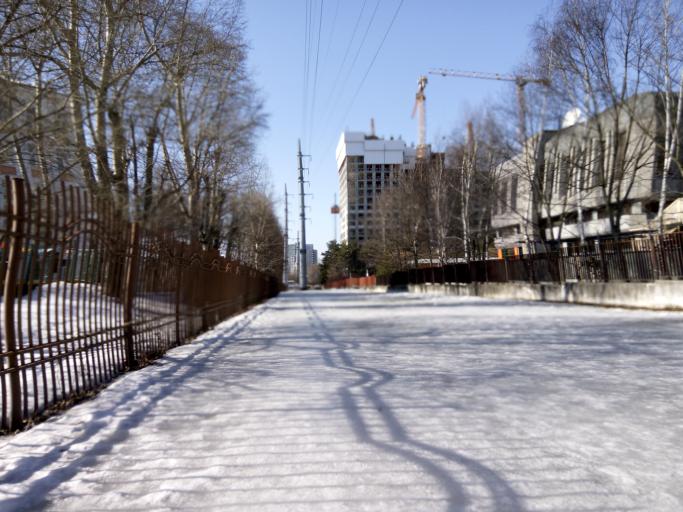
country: RU
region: Moskovskaya
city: Semenovskoye
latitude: 55.6712
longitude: 37.5267
